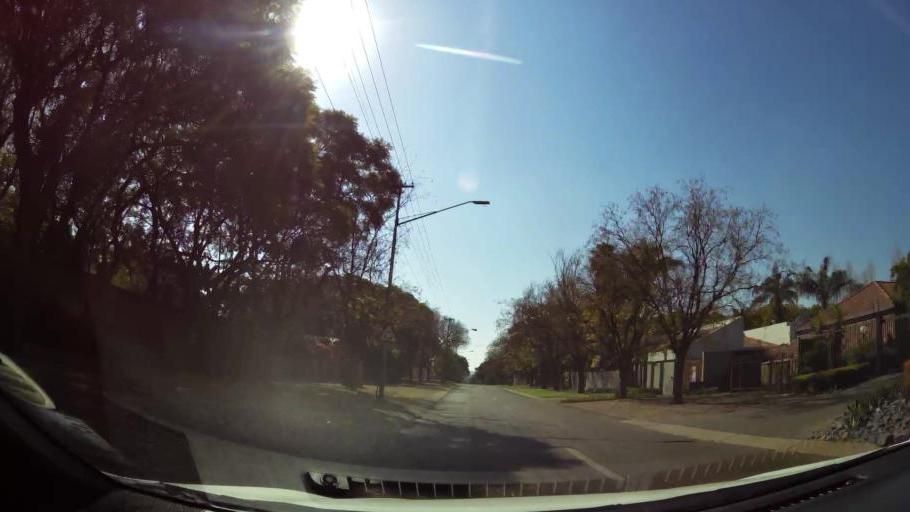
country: ZA
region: Gauteng
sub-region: City of Tshwane Metropolitan Municipality
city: Pretoria
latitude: -25.7653
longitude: 28.2391
